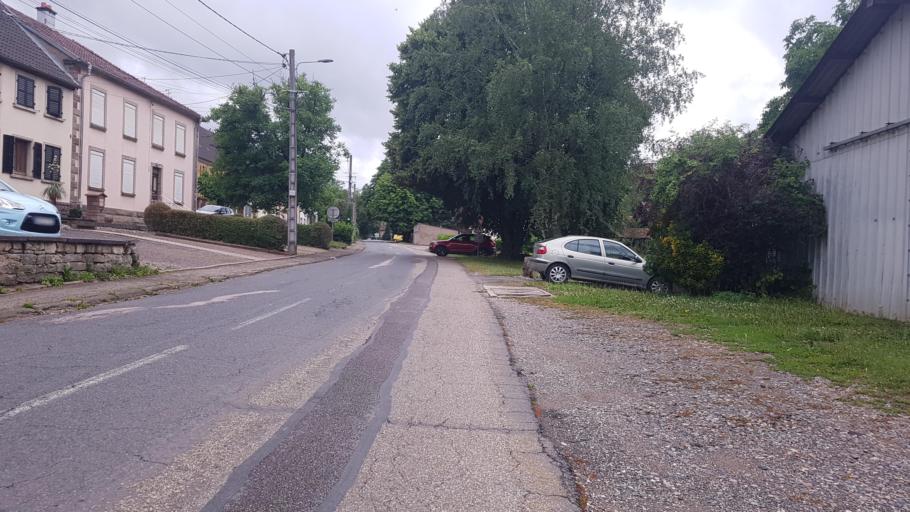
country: FR
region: Lorraine
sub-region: Departement de la Moselle
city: Niderviller
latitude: 48.7197
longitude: 7.1657
